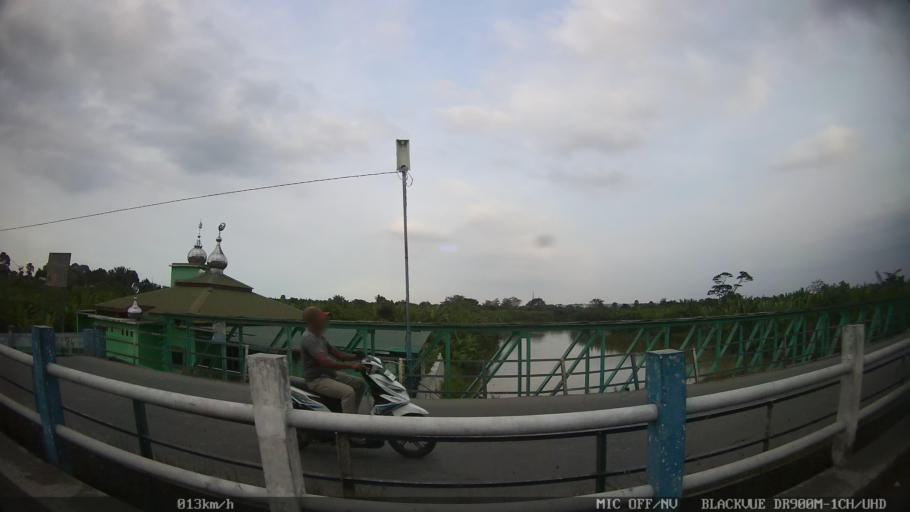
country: ID
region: North Sumatra
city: Sunggal
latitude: 3.5648
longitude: 98.6091
